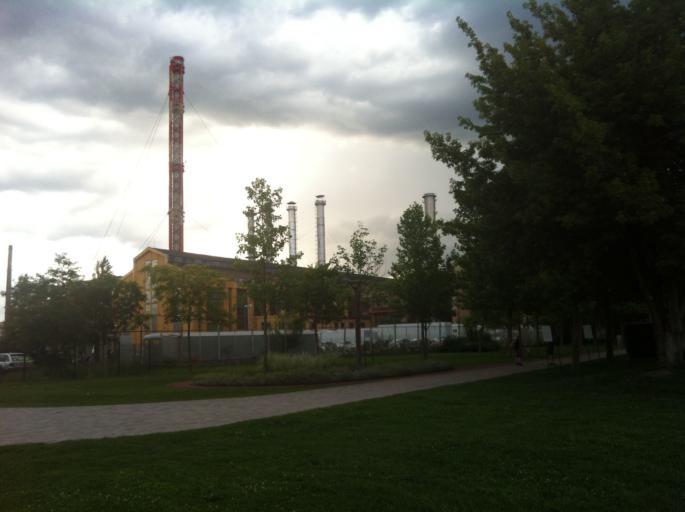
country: HU
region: Budapest
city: Budapest IX. keruelet
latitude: 47.4604
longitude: 19.0574
